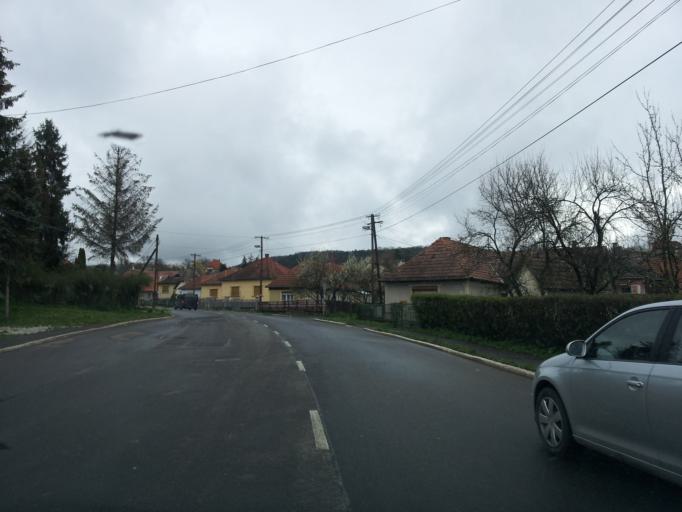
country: HU
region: Borsod-Abauj-Zemplen
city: Rudabanya
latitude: 48.4671
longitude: 20.5027
